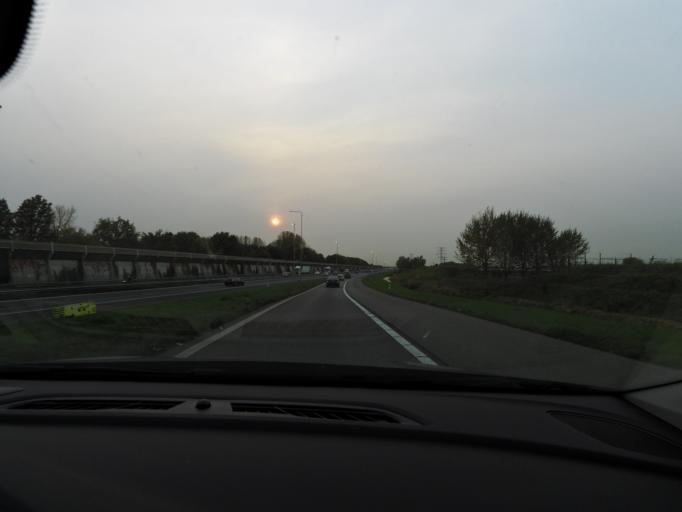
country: NL
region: Gelderland
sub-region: Gemeente Tiel
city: Tiel
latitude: 51.9012
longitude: 5.4293
